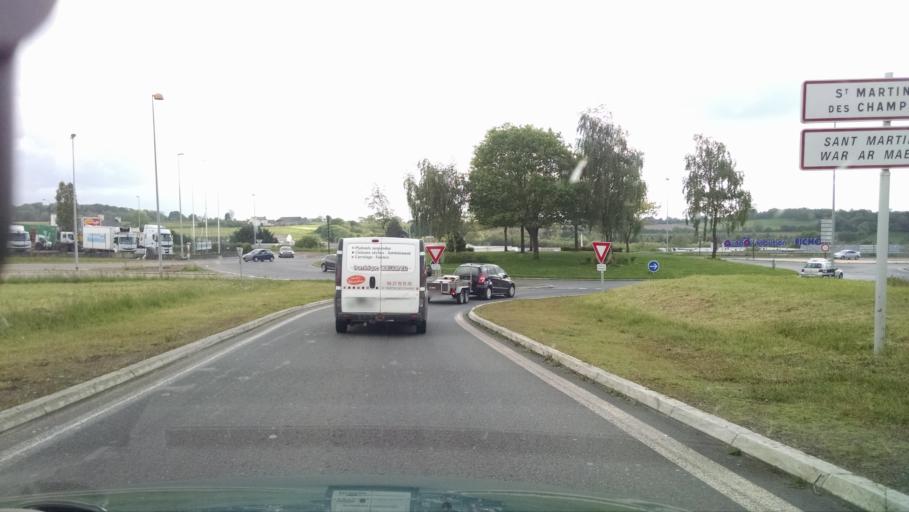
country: FR
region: Brittany
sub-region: Departement du Finistere
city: Morlaix
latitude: 48.5760
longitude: -3.8558
